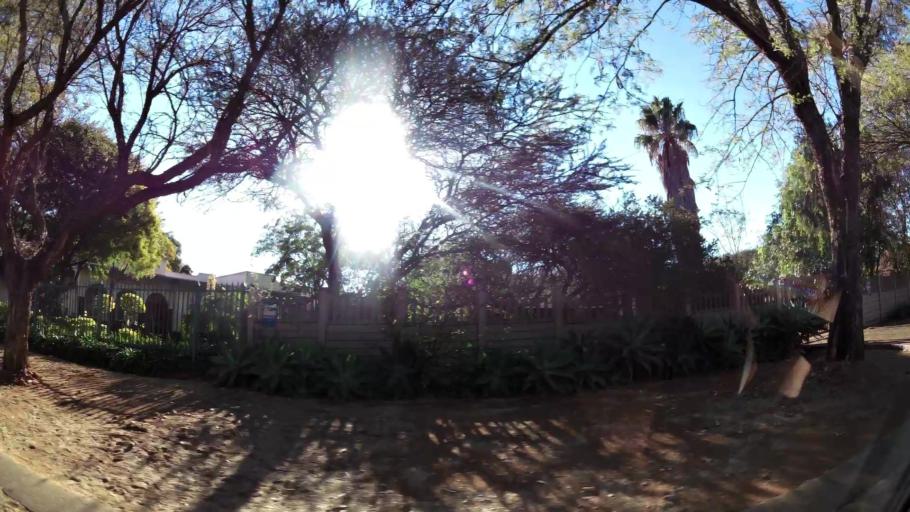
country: ZA
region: Limpopo
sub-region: Capricorn District Municipality
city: Polokwane
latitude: -23.8910
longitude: 29.4875
